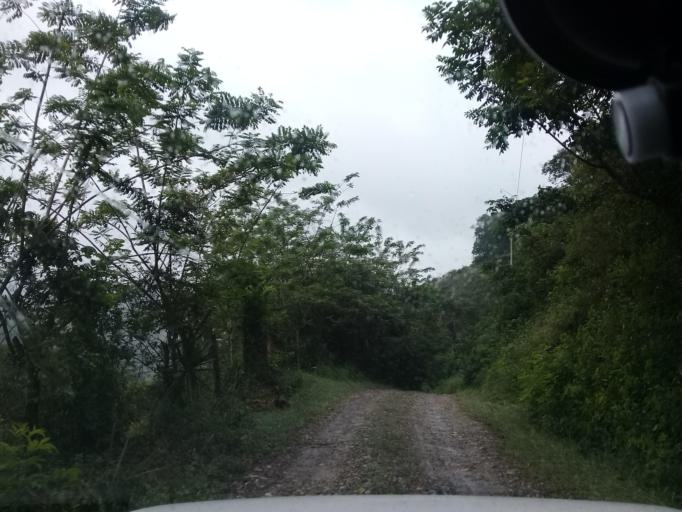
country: MX
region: Veracruz
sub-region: Chalma
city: San Pedro Coyutla
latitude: 21.2457
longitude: -98.4168
